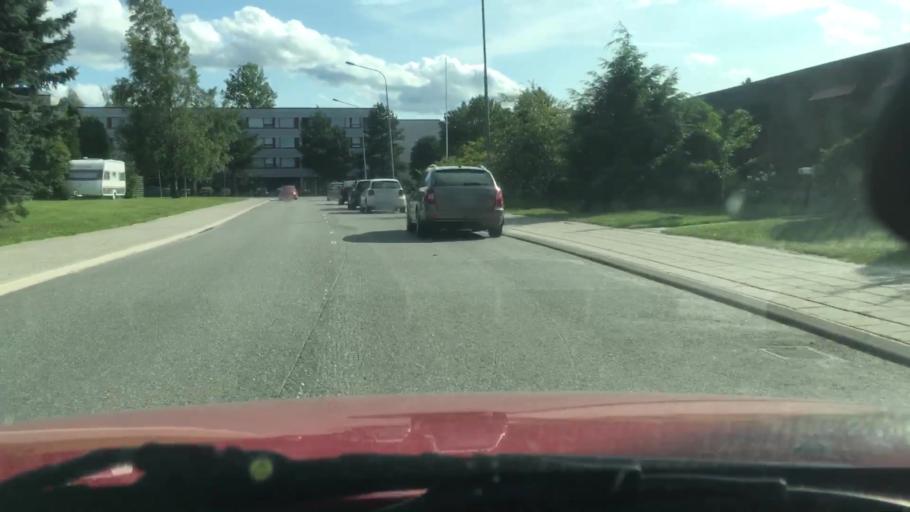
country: FI
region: Varsinais-Suomi
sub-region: Turku
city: Raisio
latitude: 60.4675
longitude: 22.2169
